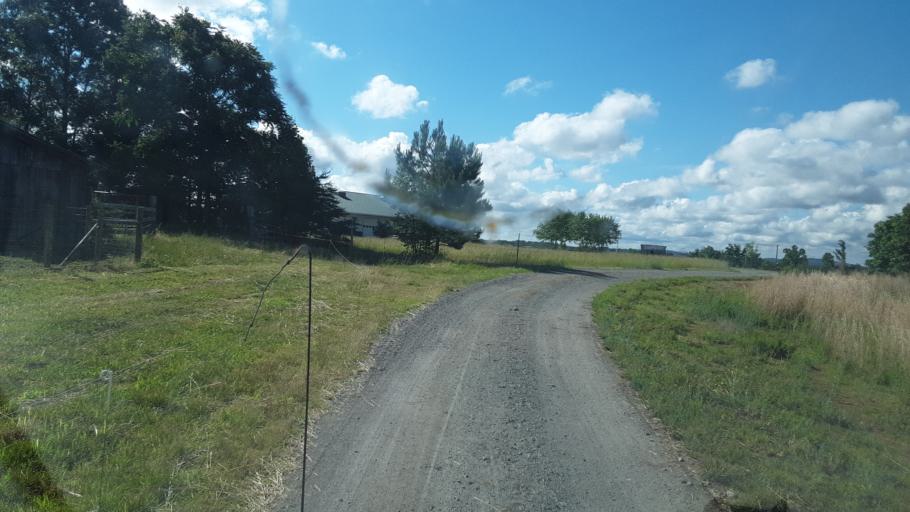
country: US
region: Virginia
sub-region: Pittsylvania County
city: Chatham
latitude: 36.8362
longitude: -79.4164
